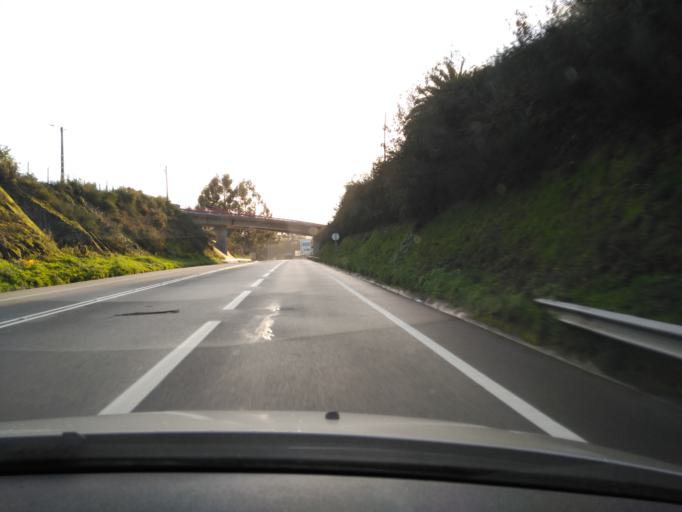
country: PT
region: Braga
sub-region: Fafe
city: Fafe
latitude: 41.4586
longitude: -8.1493
